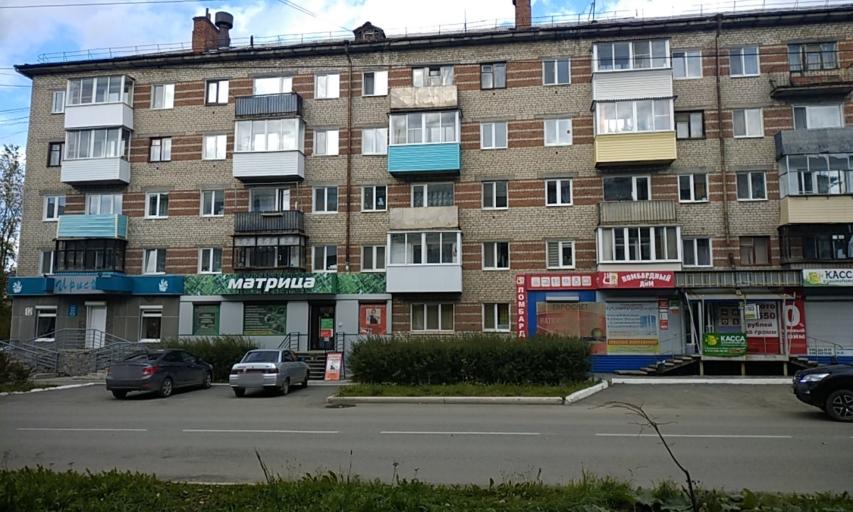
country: RU
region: Sverdlovsk
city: Krasnoural'sk
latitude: 58.3554
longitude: 60.0445
